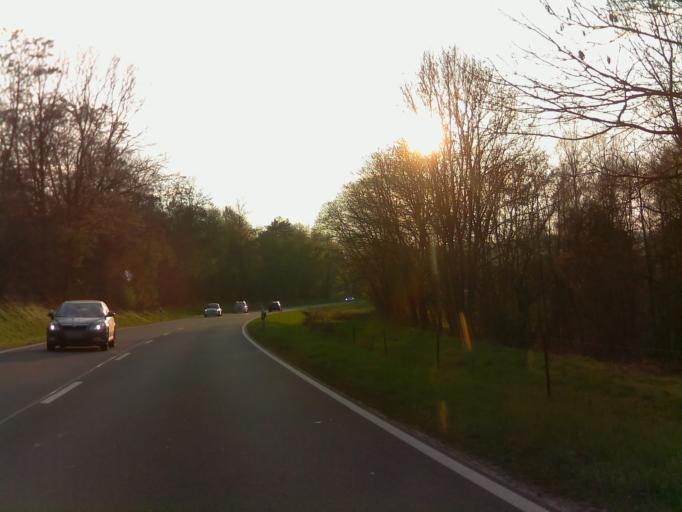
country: DE
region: Hesse
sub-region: Regierungsbezirk Kassel
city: Friedewald
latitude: 50.8625
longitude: 9.9292
